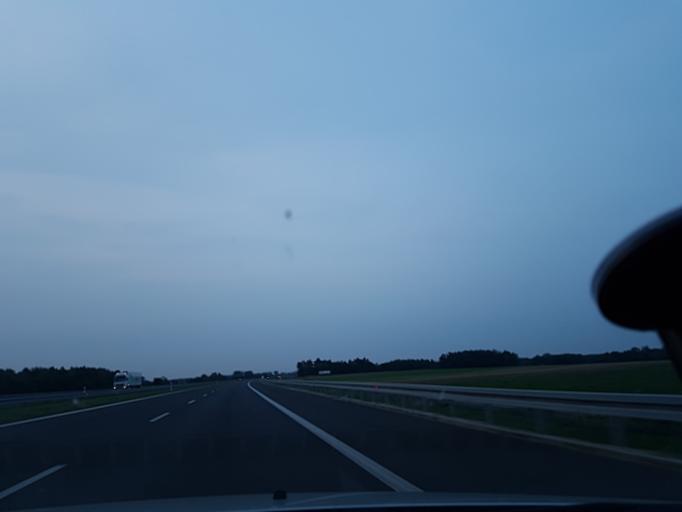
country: PL
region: Lodz Voivodeship
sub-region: Powiat zgierski
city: Strykow
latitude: 51.9484
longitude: 19.6057
